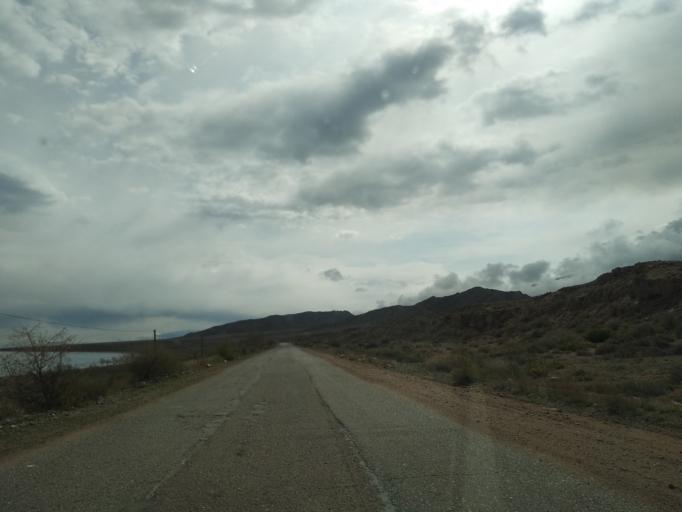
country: KG
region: Ysyk-Koel
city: Kadzhi-Say
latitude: 42.1722
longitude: 77.2555
